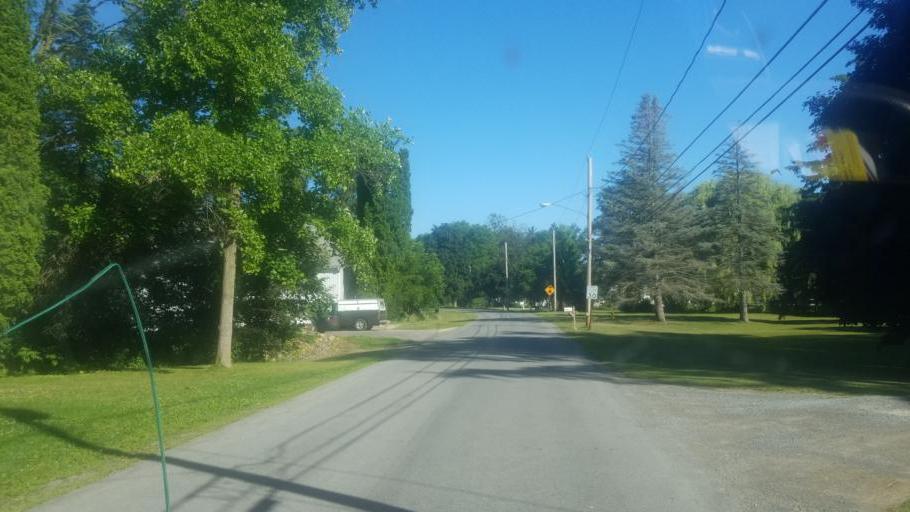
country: US
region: New York
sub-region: Ontario County
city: Phelps
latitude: 42.8892
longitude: -77.0984
